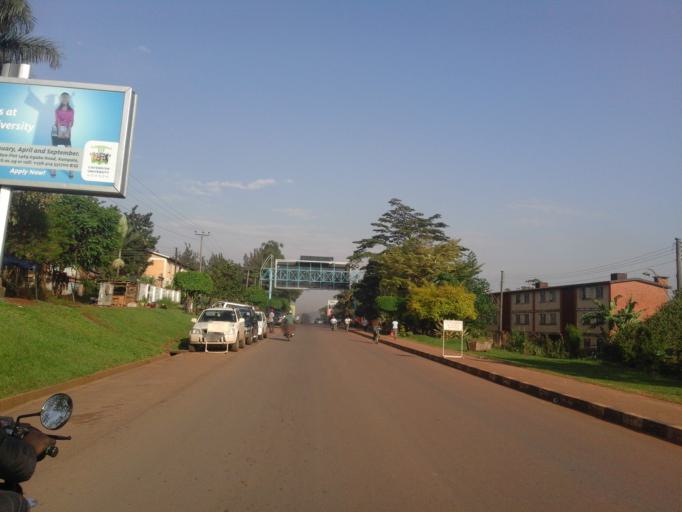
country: UG
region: Central Region
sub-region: Kampala District
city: Kampala
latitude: 0.3012
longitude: 32.5916
